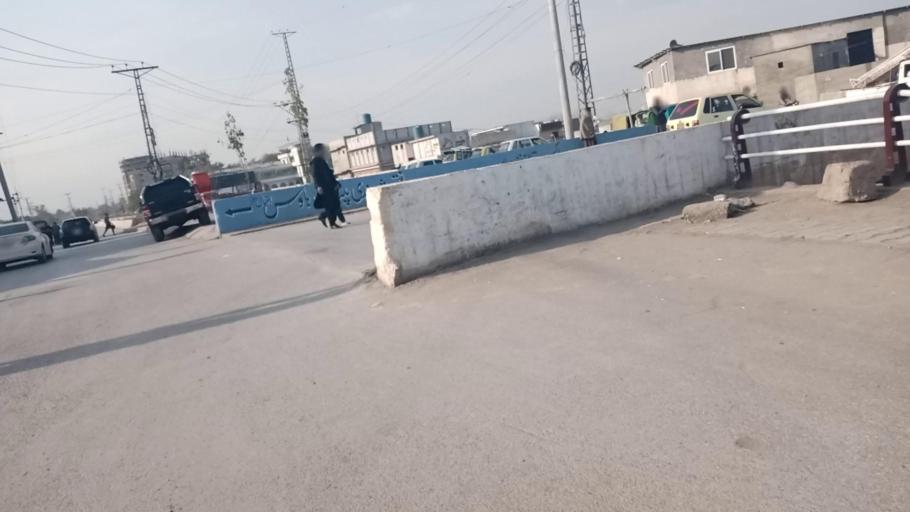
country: PK
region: Khyber Pakhtunkhwa
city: Peshawar
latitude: 34.0029
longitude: 71.4675
